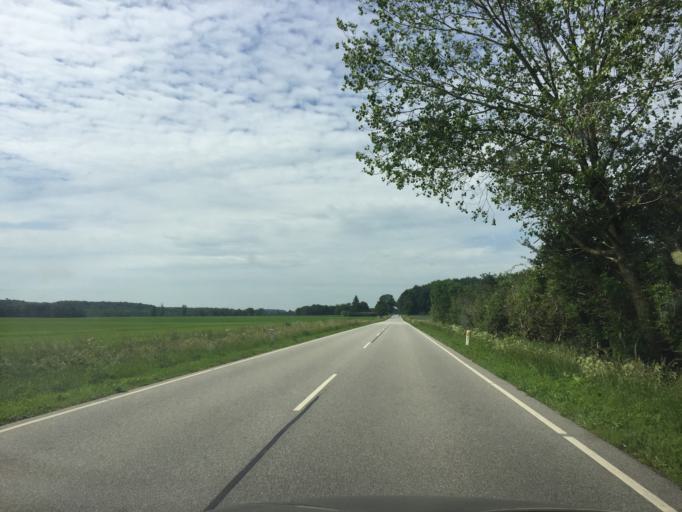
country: DK
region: South Denmark
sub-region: Nyborg Kommune
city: Ullerslev
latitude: 55.2447
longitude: 10.6592
